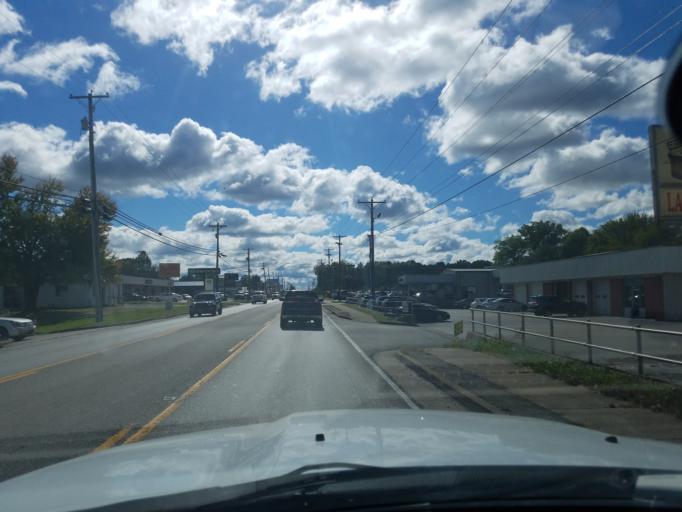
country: US
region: Kentucky
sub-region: Laurel County
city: London
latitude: 37.1010
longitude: -84.0693
